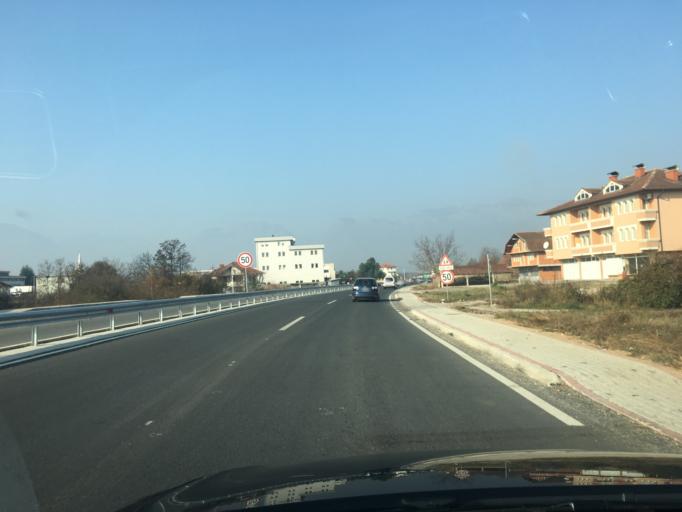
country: XK
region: Pec
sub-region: Komuna e Pejes
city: Dubova (Driloni)
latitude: 42.6549
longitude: 20.3914
